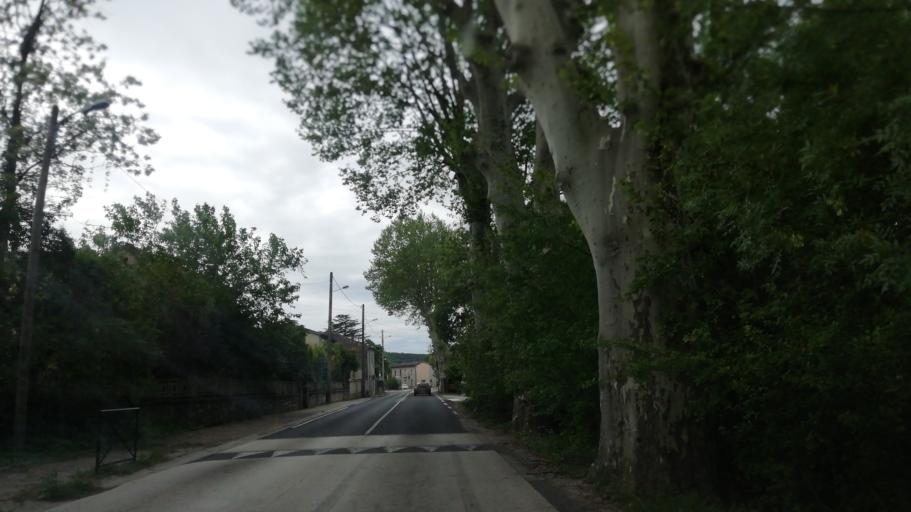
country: FR
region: Languedoc-Roussillon
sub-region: Departement de l'Herault
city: Saint-Bauzille-de-Putois
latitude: 43.9004
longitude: 3.7371
